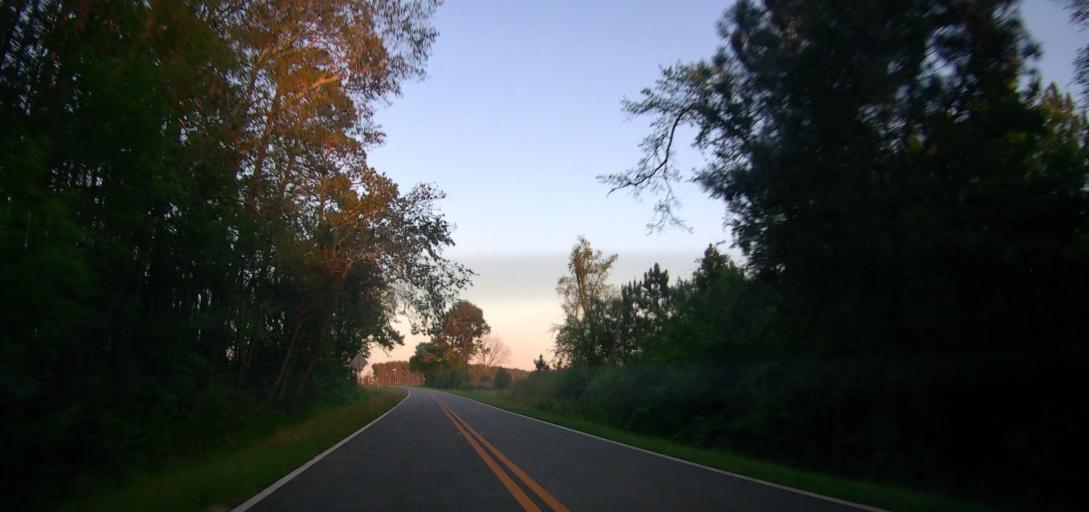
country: US
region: Georgia
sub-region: Ben Hill County
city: Fitzgerald
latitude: 31.7707
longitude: -83.3804
